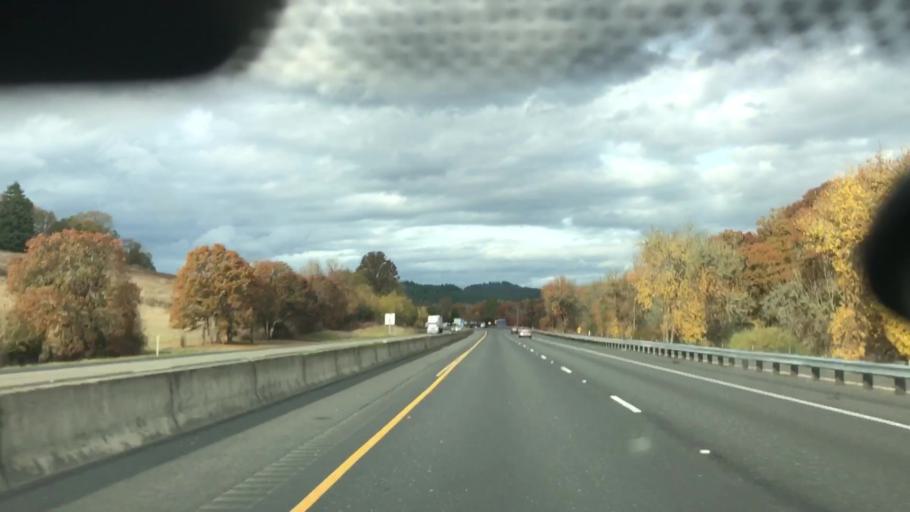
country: US
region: Oregon
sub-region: Douglas County
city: Sutherlin
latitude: 43.4652
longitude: -123.3185
